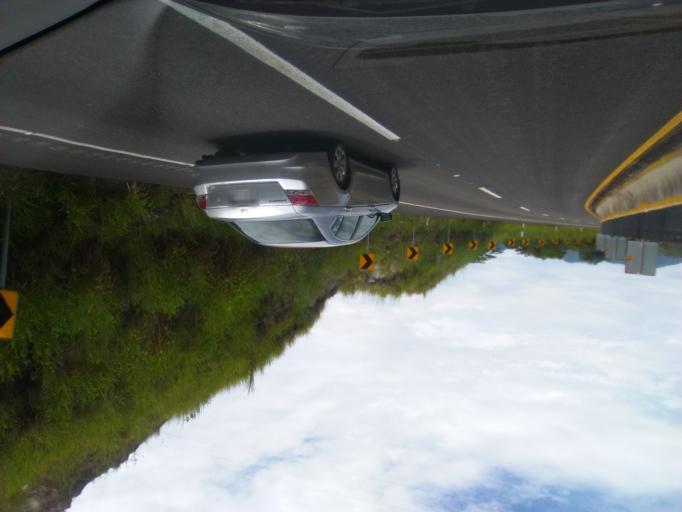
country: MX
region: Guerrero
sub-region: Chilpancingo de los Bravo
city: Cajelitos
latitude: 17.3118
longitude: -99.4896
